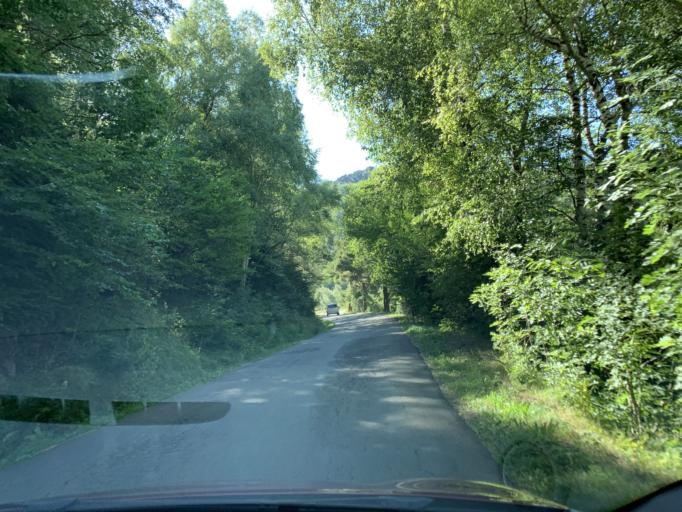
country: ES
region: Aragon
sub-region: Provincia de Huesca
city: Hoz de Jaca
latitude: 42.6918
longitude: -0.3291
